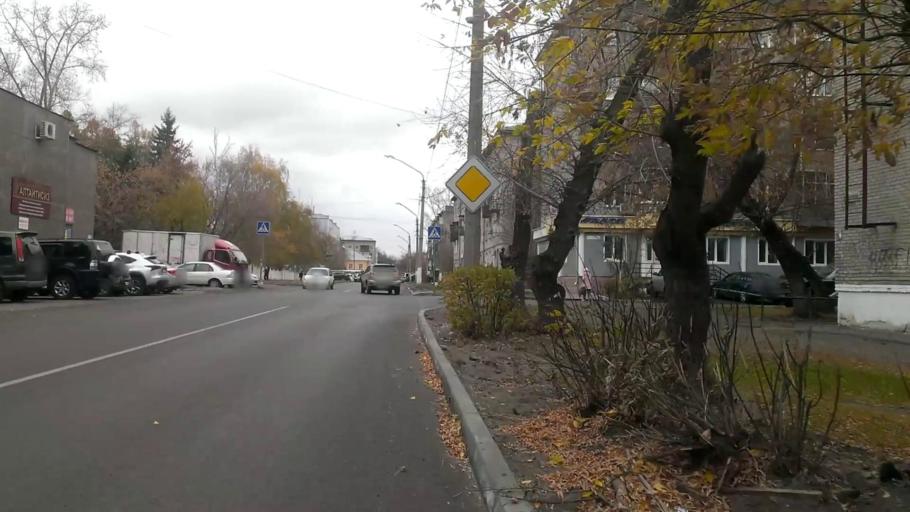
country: RU
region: Altai Krai
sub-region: Gorod Barnaulskiy
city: Barnaul
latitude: 53.3511
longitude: 83.7697
